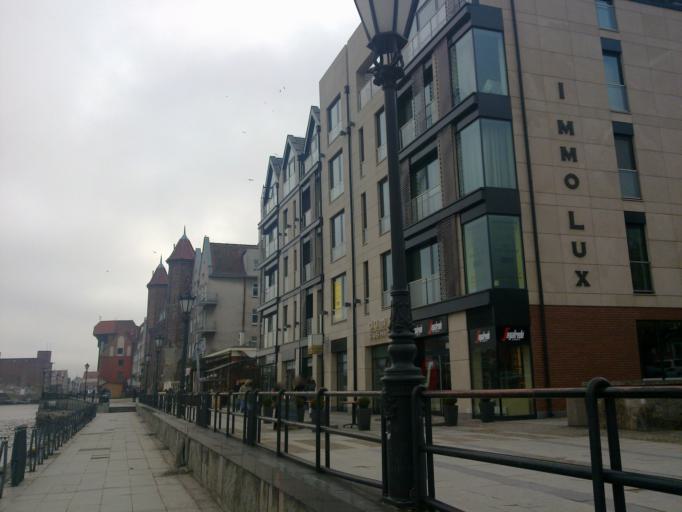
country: PL
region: Pomeranian Voivodeship
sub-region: Gdansk
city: Gdansk
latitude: 54.3529
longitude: 18.6581
